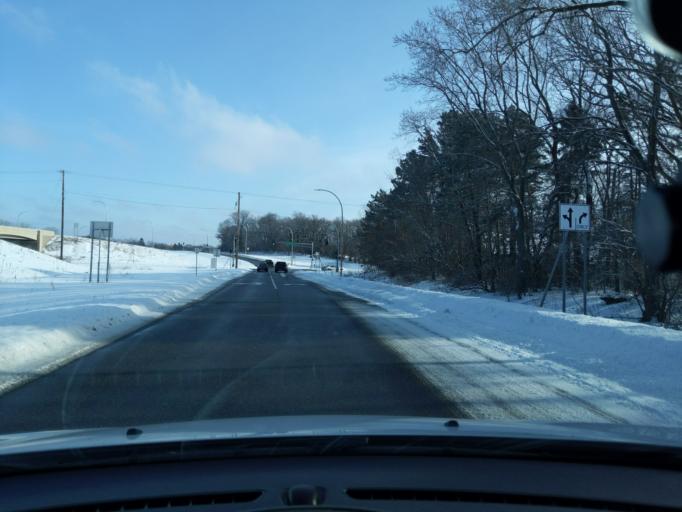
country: US
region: Minnesota
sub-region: Ramsey County
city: Roseville
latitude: 45.0098
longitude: -93.1479
